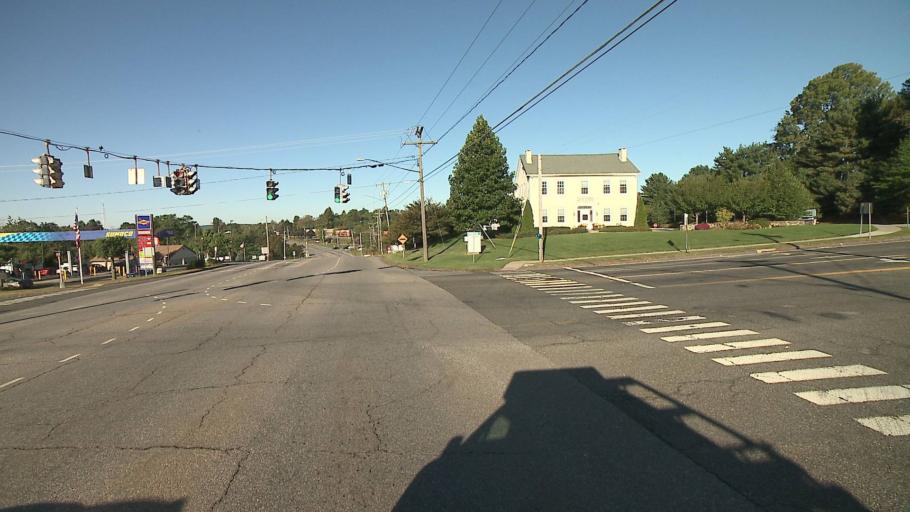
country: US
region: Connecticut
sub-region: Litchfield County
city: Northwest Harwinton
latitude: 41.8211
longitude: -73.0807
